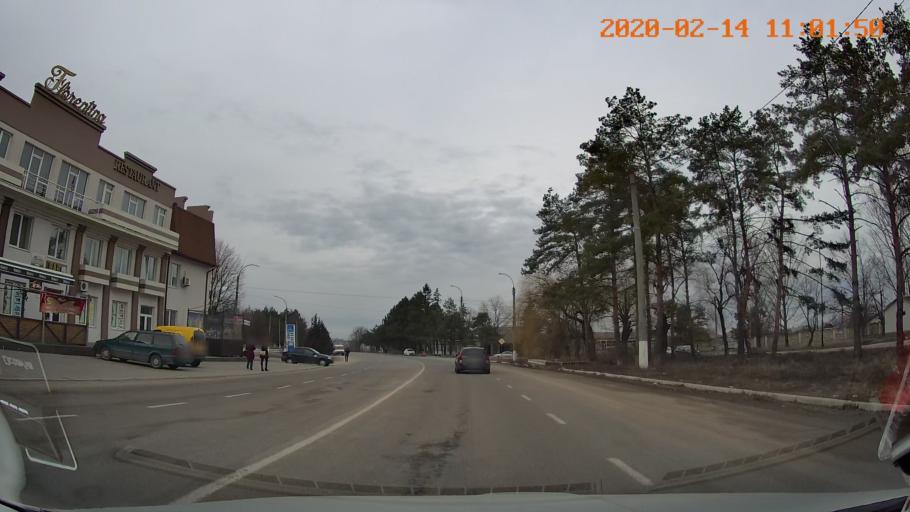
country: MD
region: Raionul Edinet
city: Edinet
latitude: 48.1620
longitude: 27.3256
